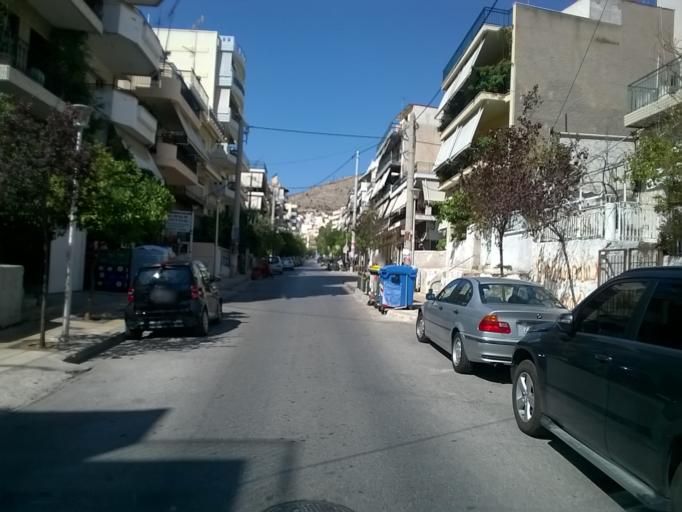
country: GR
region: Attica
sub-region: Nomos Piraios
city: Keratsini
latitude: 37.9697
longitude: 23.6253
